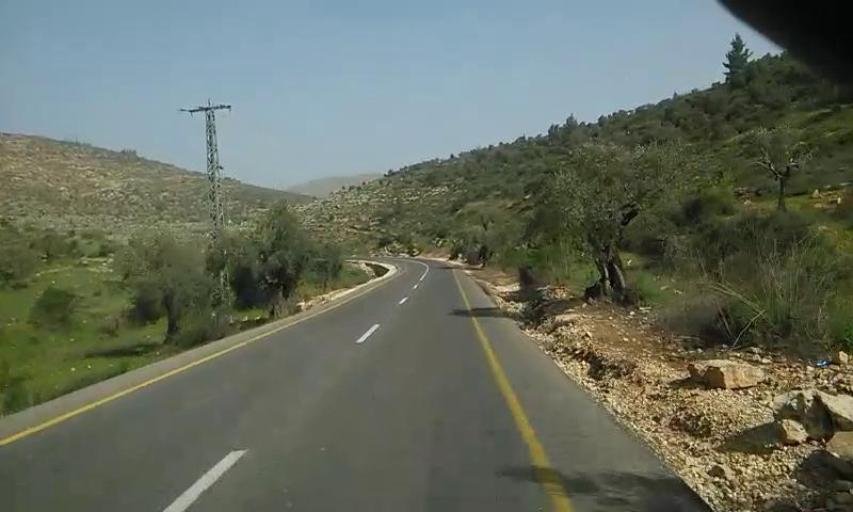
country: PS
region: West Bank
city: `Atarah
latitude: 31.9942
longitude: 35.2273
